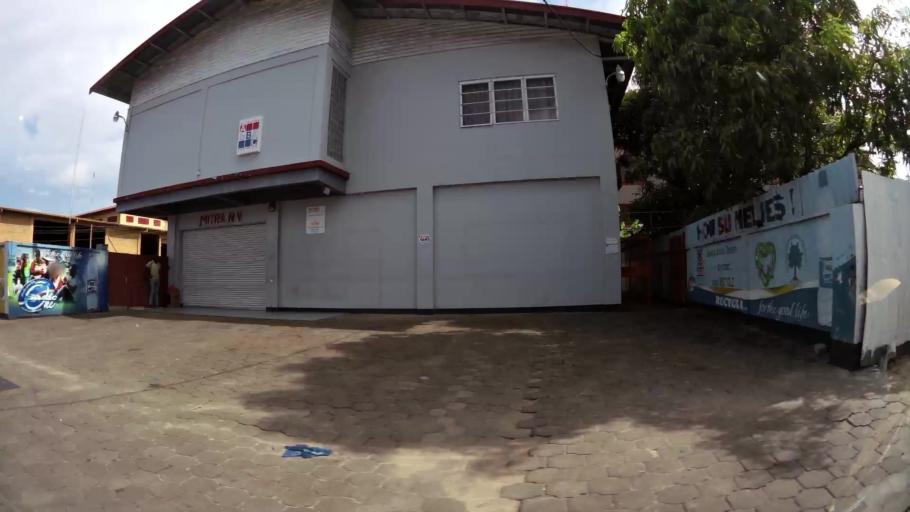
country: SR
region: Paramaribo
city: Paramaribo
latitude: 5.8356
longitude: -55.1486
